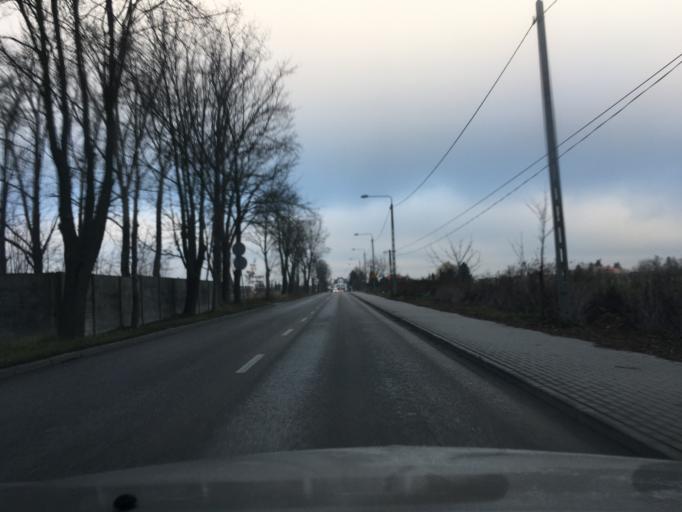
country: PL
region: Masovian Voivodeship
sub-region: Powiat piaseczynski
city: Lesznowola
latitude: 52.0839
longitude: 20.9401
